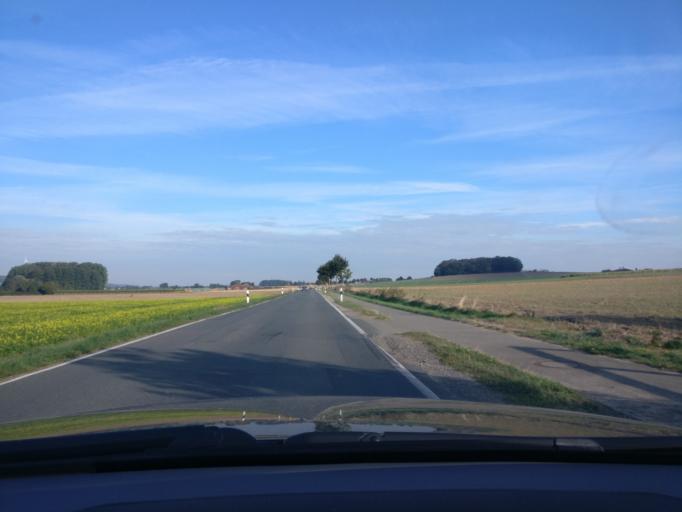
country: DE
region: Lower Saxony
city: Melle
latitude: 52.1967
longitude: 8.2759
